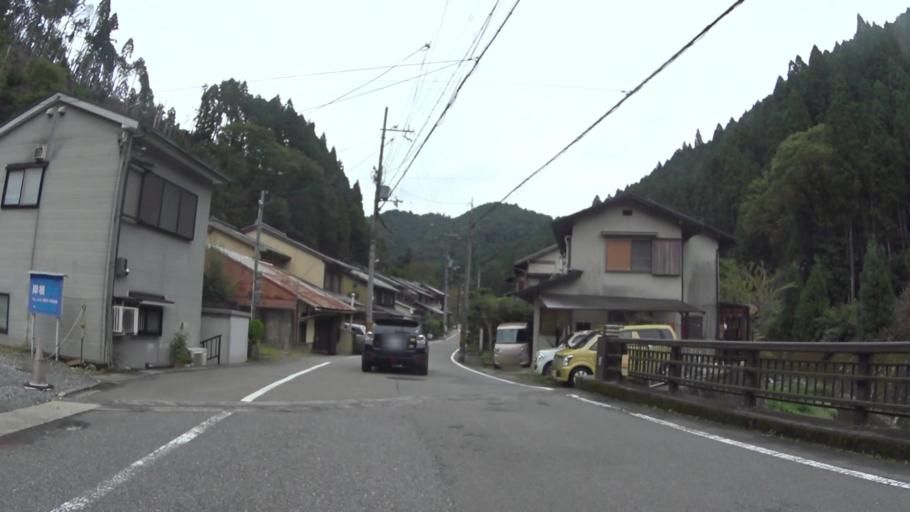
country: JP
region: Kyoto
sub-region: Kyoto-shi
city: Kamigyo-ku
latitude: 35.1110
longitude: 135.7693
